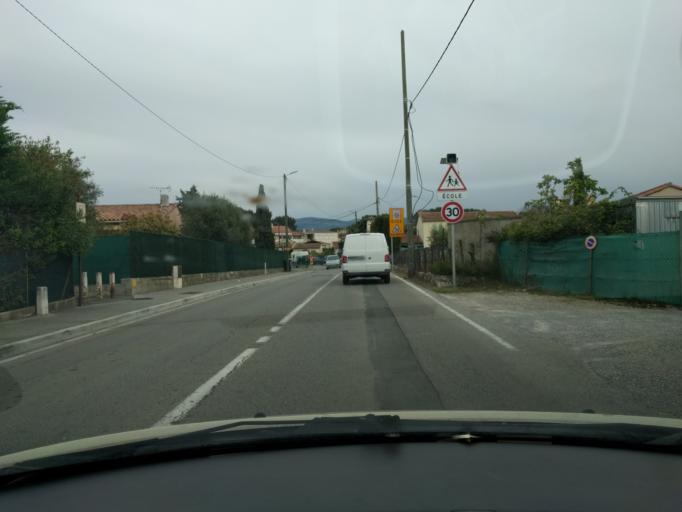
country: FR
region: Provence-Alpes-Cote d'Azur
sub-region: Departement des Alpes-Maritimes
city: La Roquette-sur-Siagne
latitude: 43.5956
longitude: 6.9563
